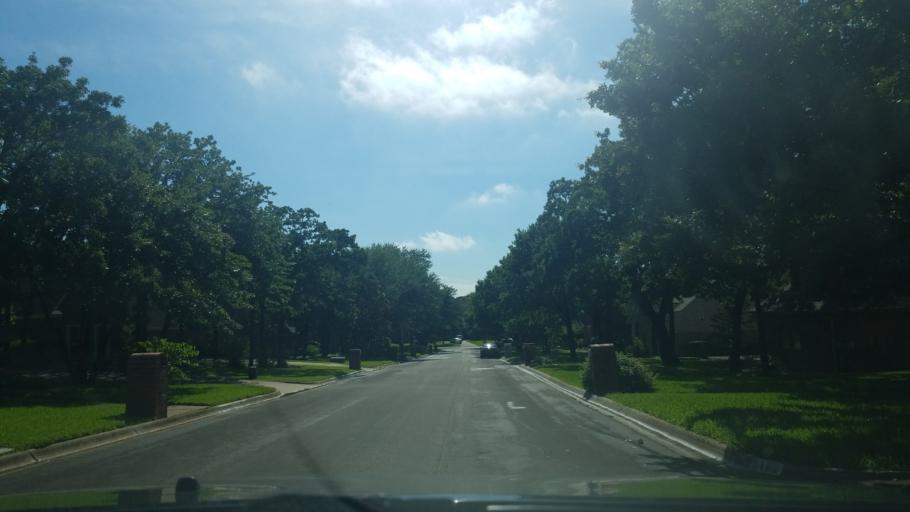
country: US
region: Texas
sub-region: Denton County
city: Denton
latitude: 33.1796
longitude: -97.1150
